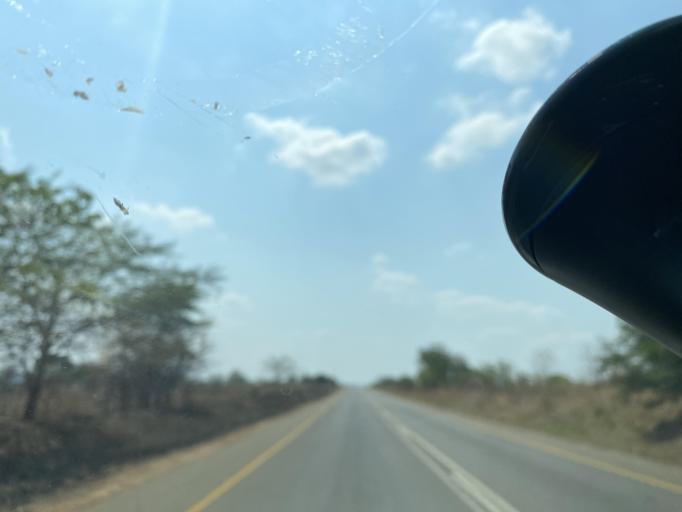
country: ZM
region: Lusaka
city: Chongwe
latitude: -15.5513
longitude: 28.6772
